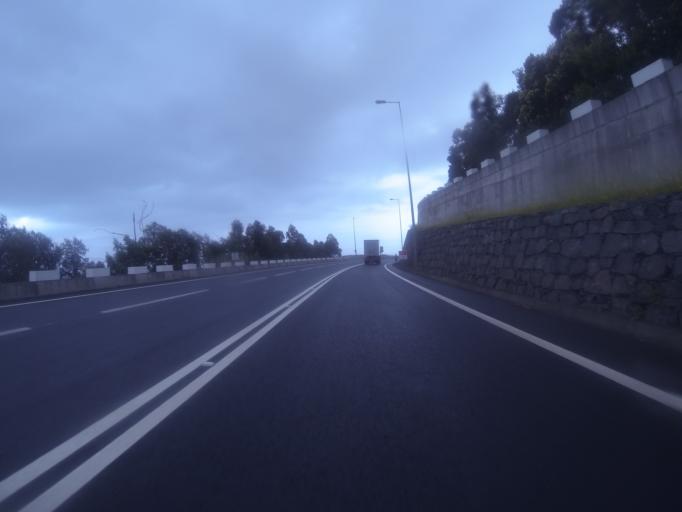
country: PT
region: Madeira
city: Canico
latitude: 32.6532
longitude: -16.8507
